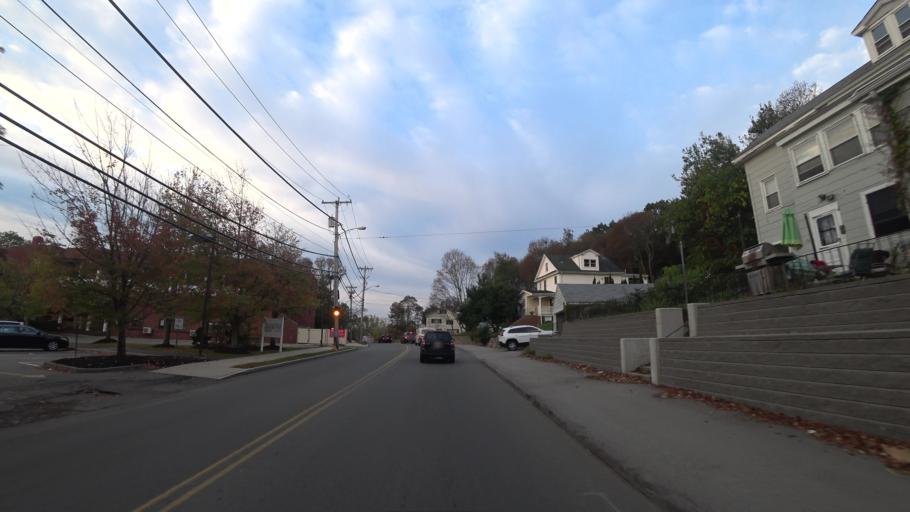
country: US
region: Massachusetts
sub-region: Essex County
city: Saugus
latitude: 42.4391
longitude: -71.0176
